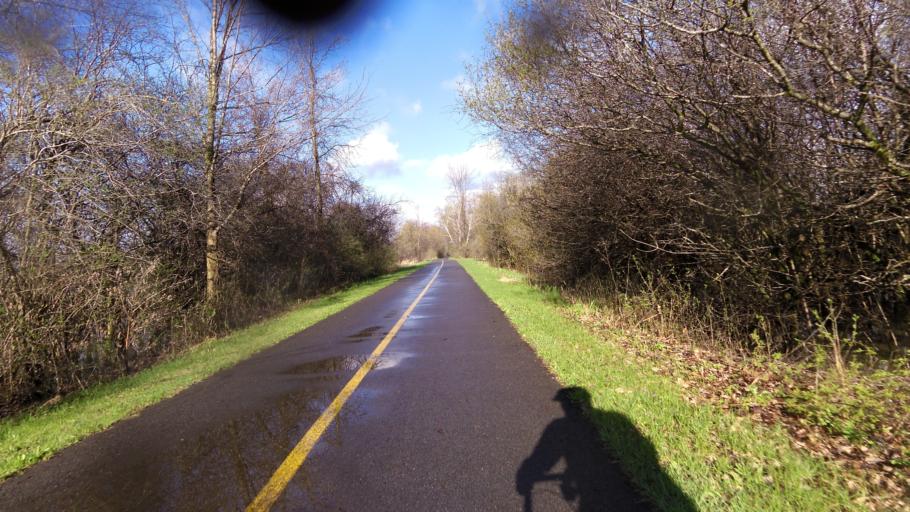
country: CA
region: Ontario
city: Bells Corners
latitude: 45.3420
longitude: -75.8499
